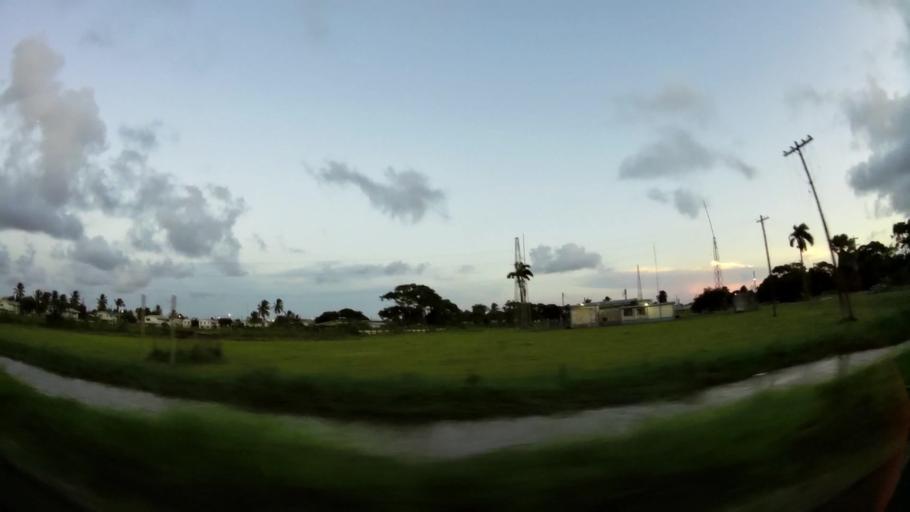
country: GY
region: Demerara-Mahaica
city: Georgetown
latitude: 6.8240
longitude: -58.1478
